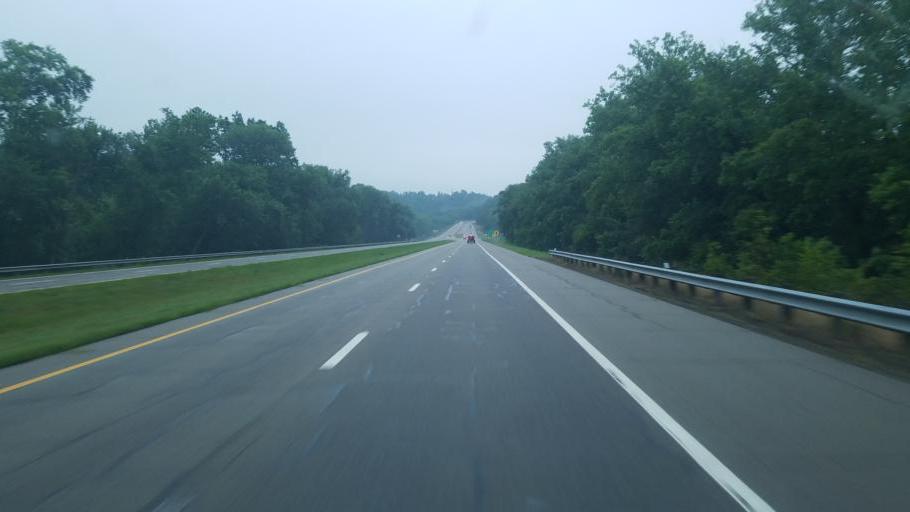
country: US
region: Ohio
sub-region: Tuscarawas County
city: Newcomerstown
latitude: 40.2822
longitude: -81.6456
